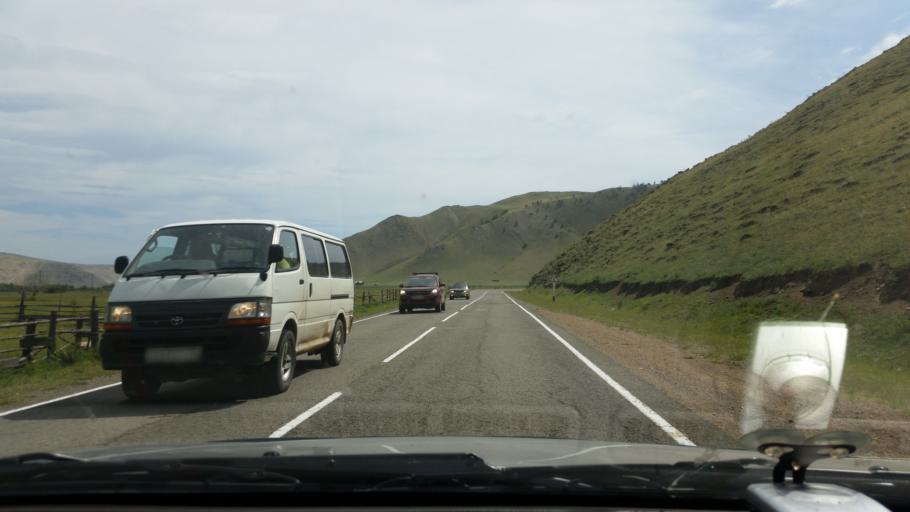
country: RU
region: Irkutsk
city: Yelantsy
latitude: 52.8060
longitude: 106.4676
